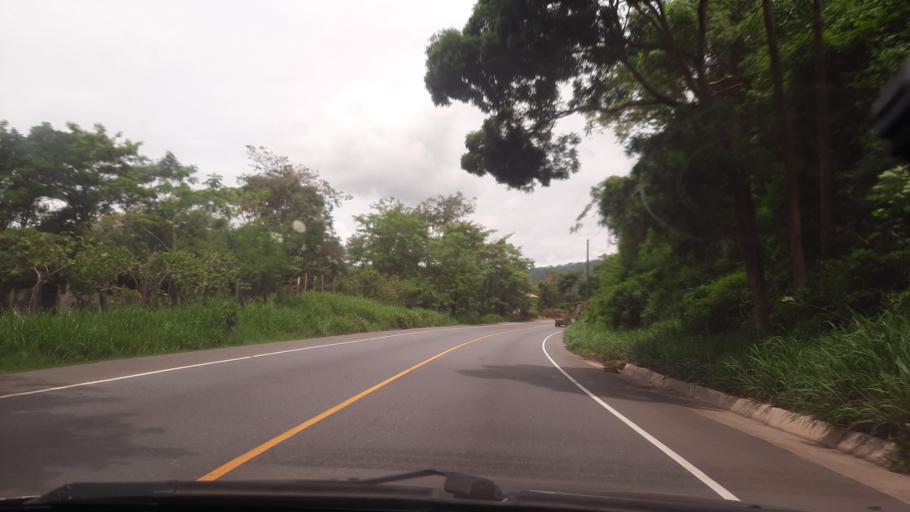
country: GT
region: Izabal
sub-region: Municipio de Los Amates
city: Los Amates
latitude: 15.2127
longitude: -89.2375
